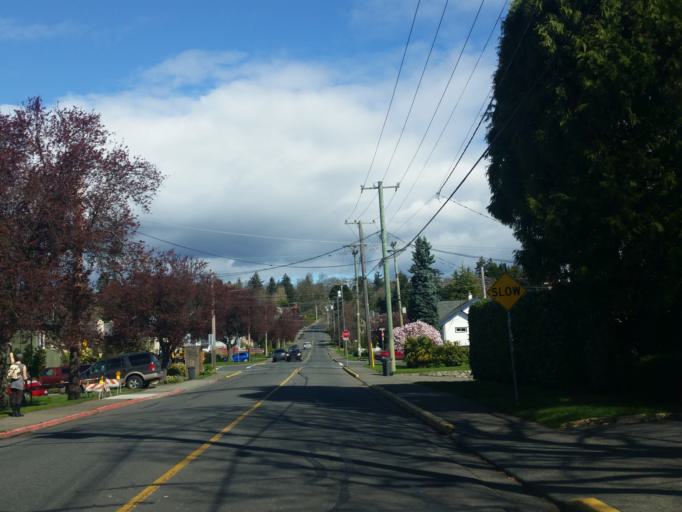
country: CA
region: British Columbia
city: Victoria
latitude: 48.4266
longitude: -123.4078
